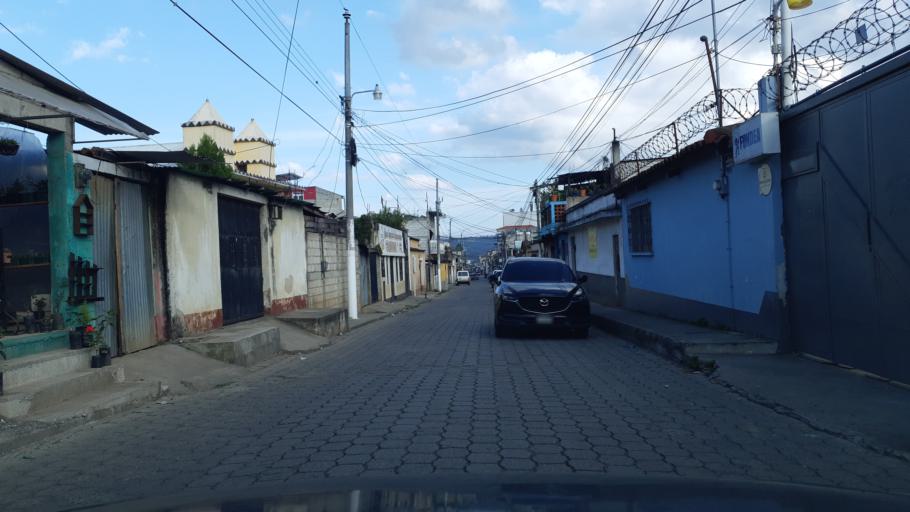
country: GT
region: Chimaltenango
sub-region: Municipio de Chimaltenango
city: Chimaltenango
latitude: 14.6602
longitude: -90.8263
